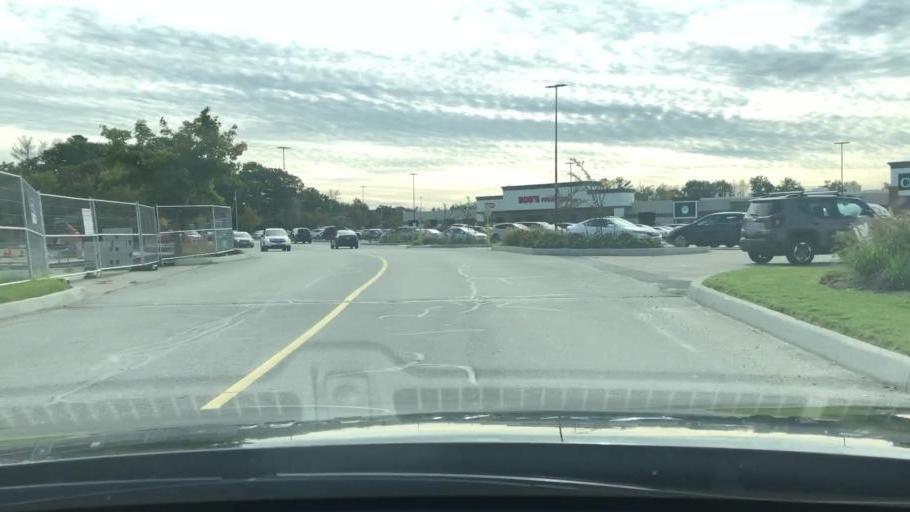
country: US
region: New Hampshire
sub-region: Rockingham County
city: Salem
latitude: 42.7665
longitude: -71.2194
